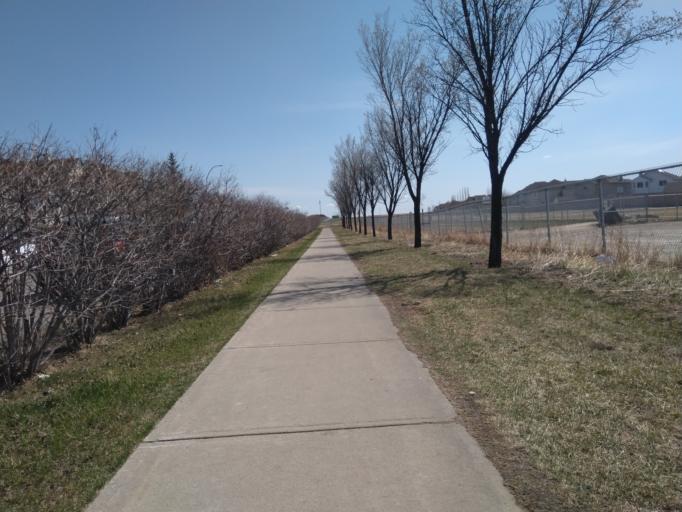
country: CA
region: Alberta
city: Chestermere
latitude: 51.1108
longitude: -113.9307
